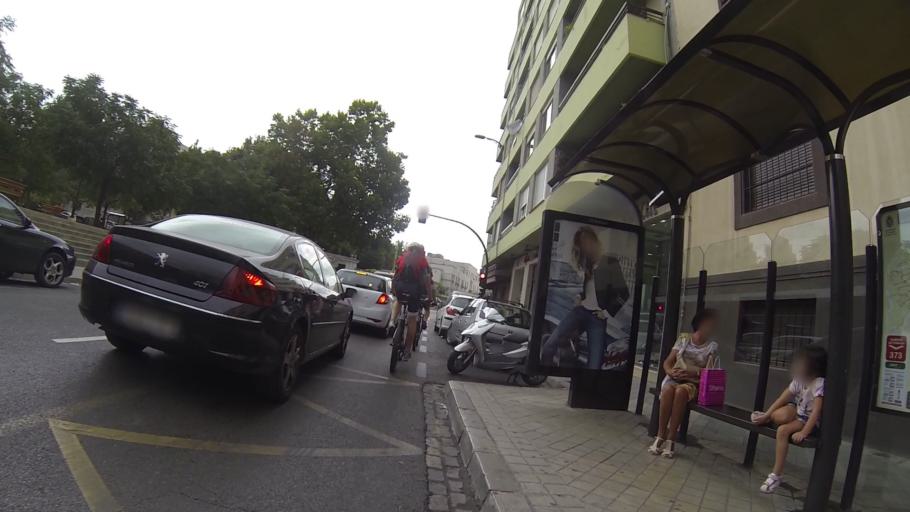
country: ES
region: Andalusia
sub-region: Provincia de Granada
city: Granada
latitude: 37.1883
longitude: -3.6077
